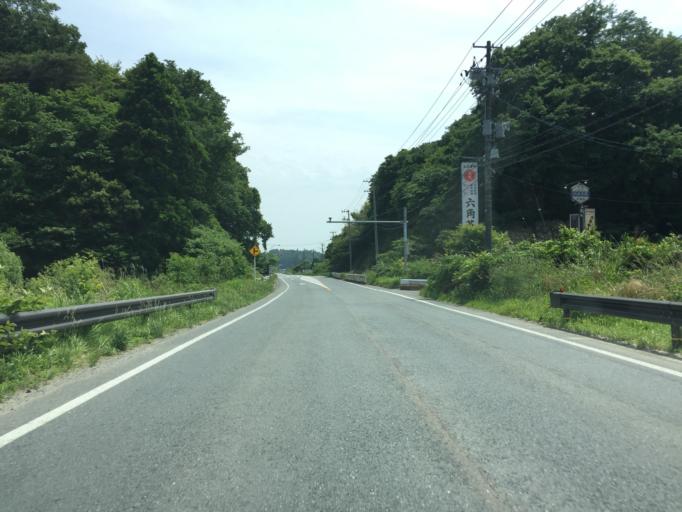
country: JP
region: Fukushima
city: Namie
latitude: 37.4730
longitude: 141.0081
